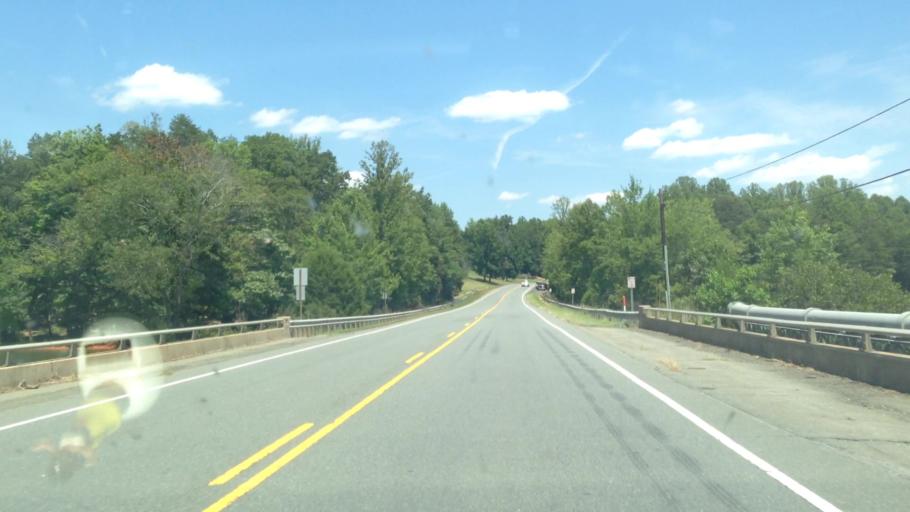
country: US
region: North Carolina
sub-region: Guilford County
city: Stokesdale
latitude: 36.2256
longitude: -80.0445
